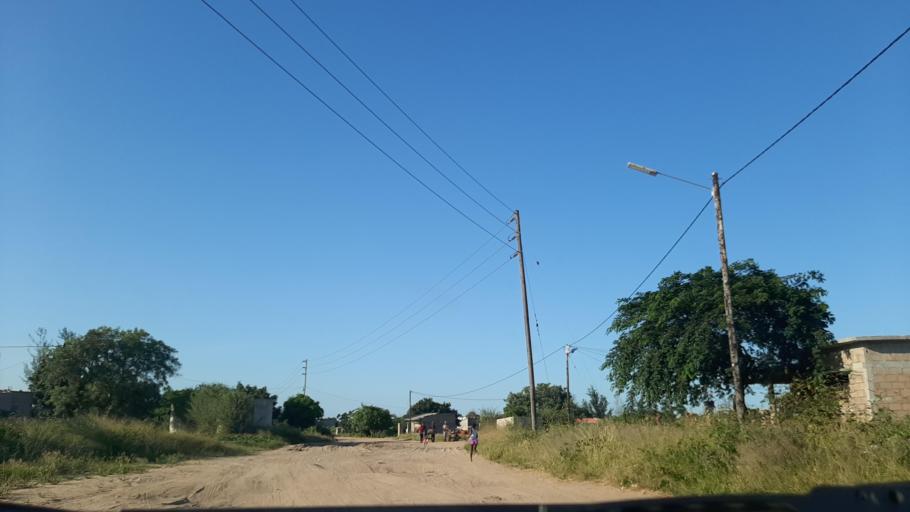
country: MZ
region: Maputo City
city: Maputo
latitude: -25.7590
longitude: 32.5501
